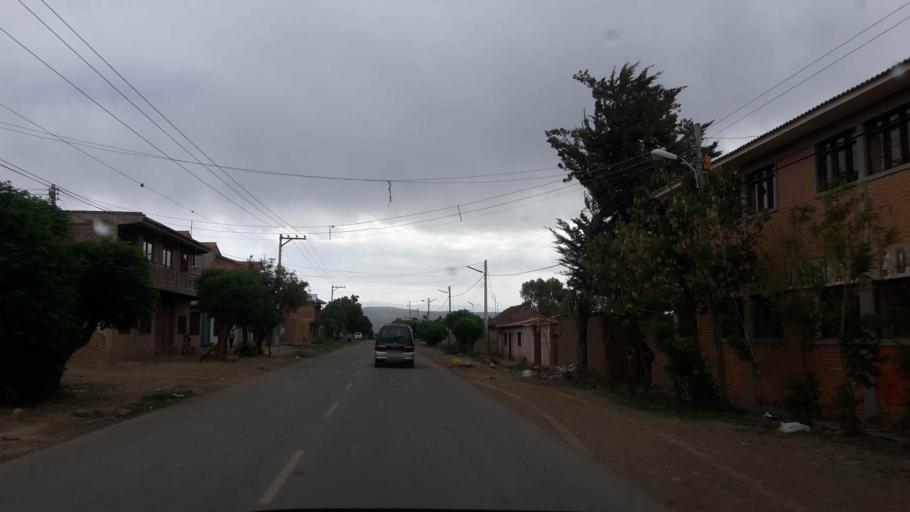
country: BO
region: Cochabamba
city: Tarata
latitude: -17.5841
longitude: -66.0527
